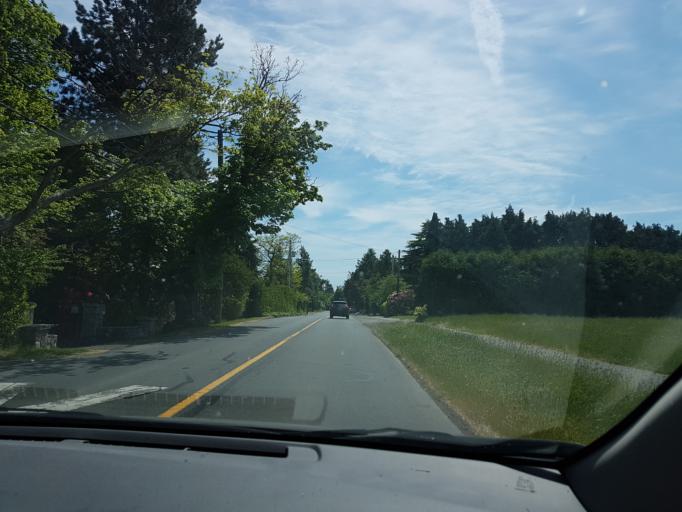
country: CA
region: British Columbia
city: Oak Bay
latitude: 48.4845
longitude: -123.3061
